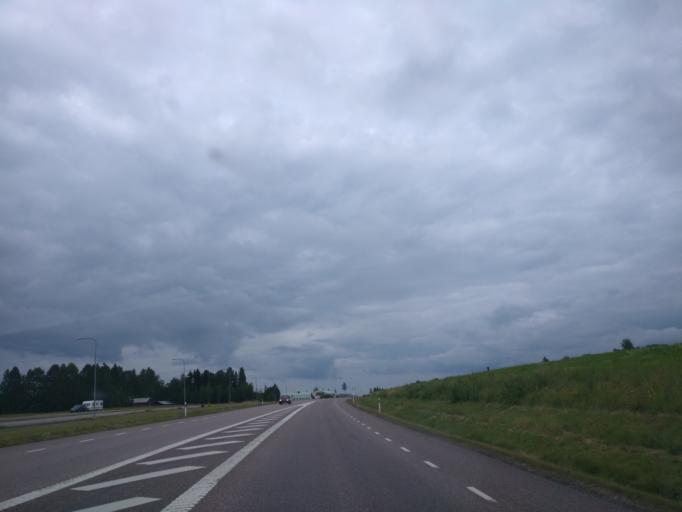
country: SE
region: Vaermland
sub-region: Sunne Kommun
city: Sunne
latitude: 59.8449
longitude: 13.1234
